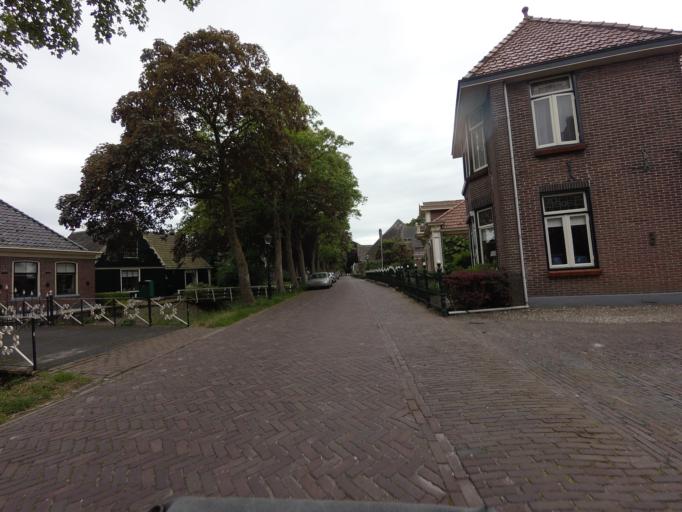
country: NL
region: North Holland
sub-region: Gemeente Medemblik
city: Opperdoes
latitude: 52.7433
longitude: 5.0598
